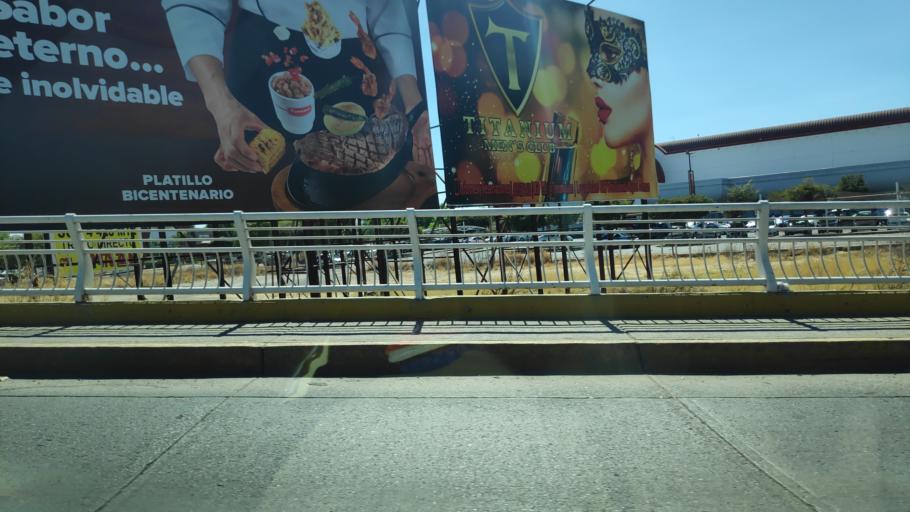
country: MX
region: Sinaloa
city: Culiacan
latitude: 24.8138
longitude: -107.4028
